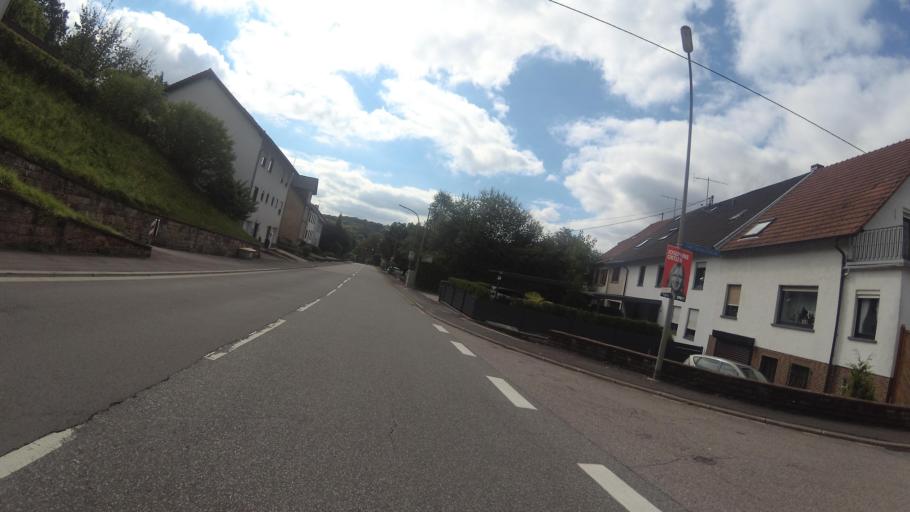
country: FR
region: Lorraine
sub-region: Departement de la Moselle
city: Freyming-Merlebach
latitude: 49.1768
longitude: 6.8115
